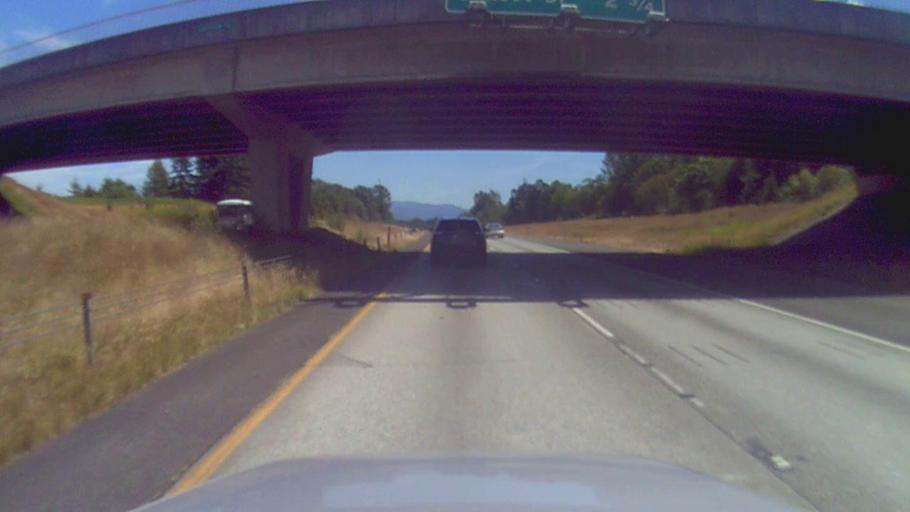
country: US
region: Washington
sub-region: Whatcom County
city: Marietta-Alderwood
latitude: 48.7882
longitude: -122.5161
